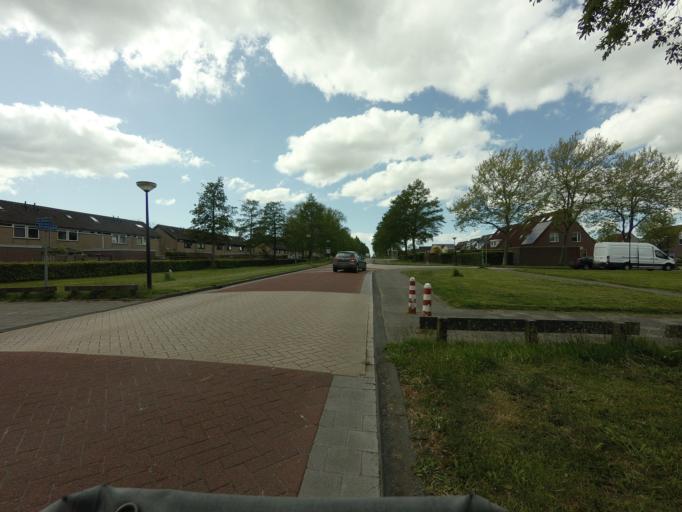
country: NL
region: Friesland
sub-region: Sudwest Fryslan
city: Bolsward
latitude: 53.0713
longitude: 5.5329
